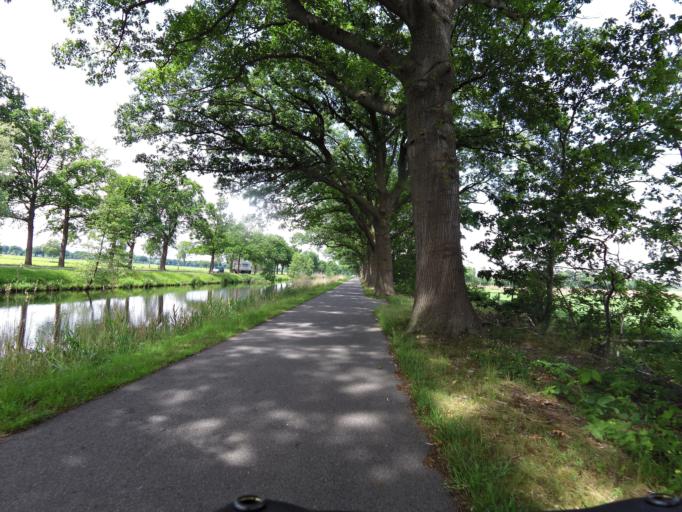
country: NL
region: Gelderland
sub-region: Gemeente Brummen
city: Eerbeek
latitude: 52.1188
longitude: 6.0651
